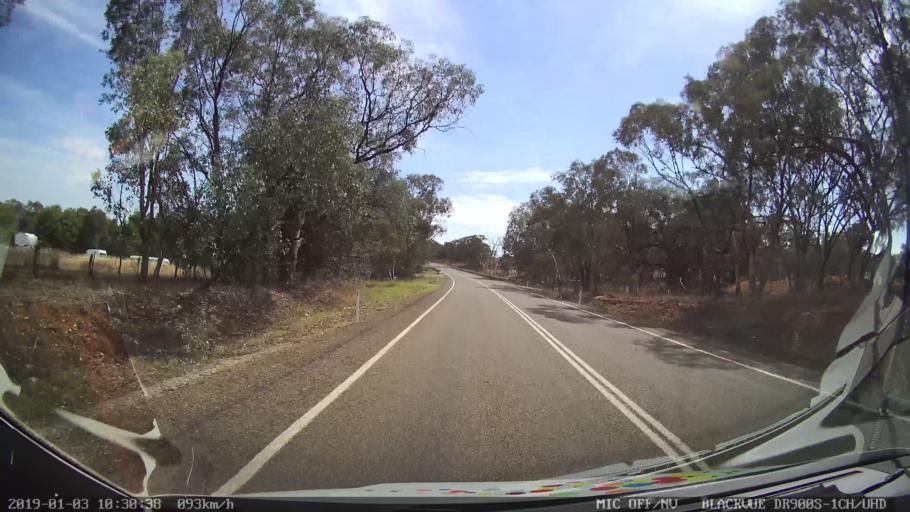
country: AU
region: New South Wales
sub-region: Young
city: Young
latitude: -34.3601
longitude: 148.2704
